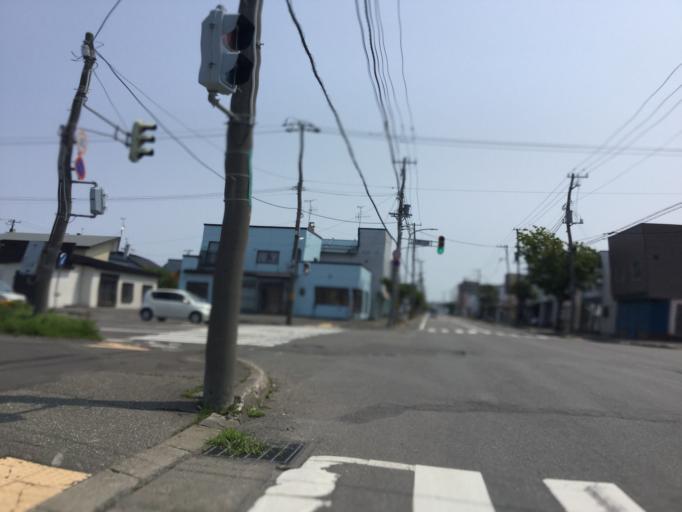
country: JP
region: Hokkaido
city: Wakkanai
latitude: 45.3959
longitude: 141.6929
